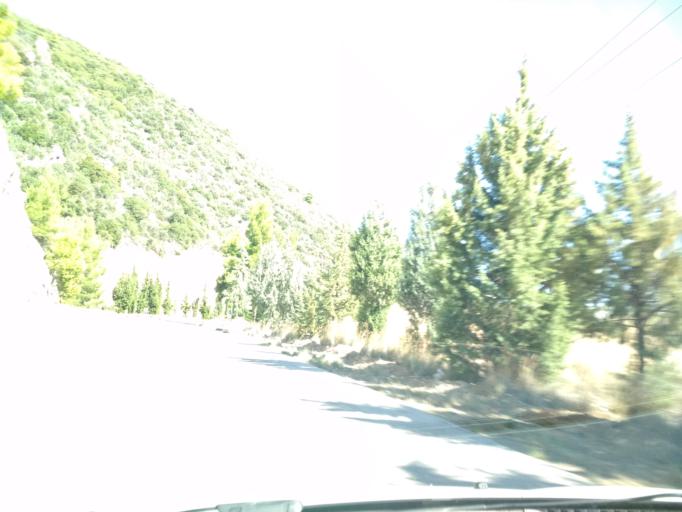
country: GR
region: Central Greece
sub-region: Nomos Evvoias
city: Oreoi
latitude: 38.8461
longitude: 23.0703
